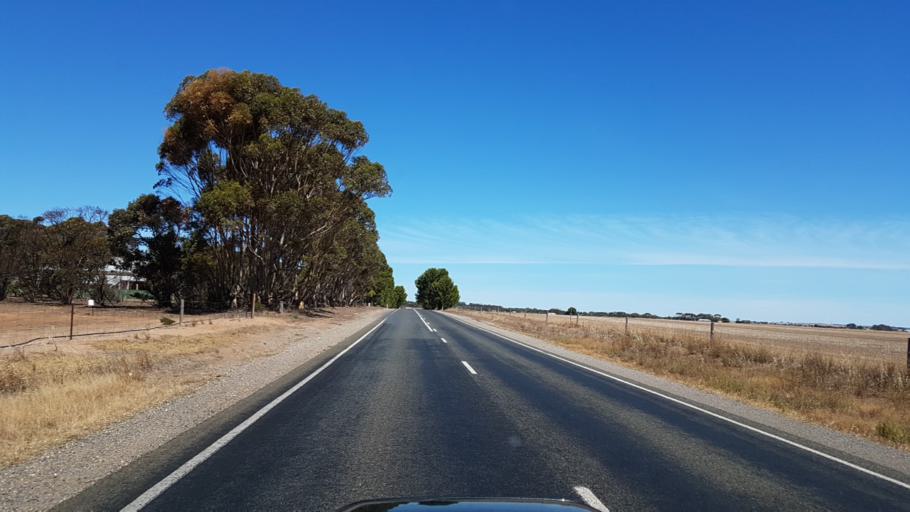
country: AU
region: South Australia
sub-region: Yorke Peninsula
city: Maitland
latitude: -34.3489
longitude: 137.6615
